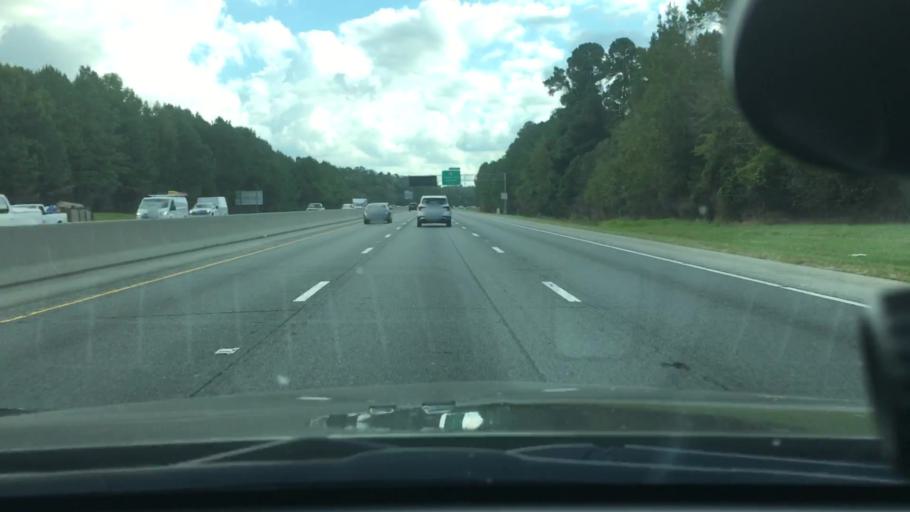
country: US
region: North Carolina
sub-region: Orange County
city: Chapel Hill
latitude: 35.9320
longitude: -78.9886
